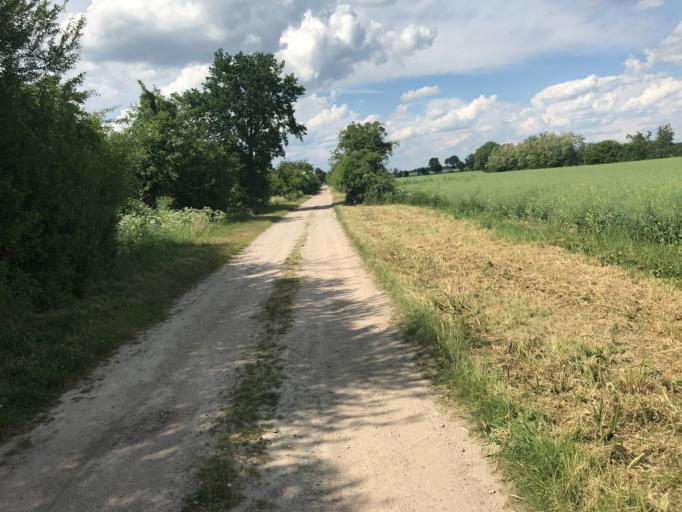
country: PL
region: West Pomeranian Voivodeship
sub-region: Powiat mysliborski
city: Debno
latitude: 52.7640
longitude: 14.6388
